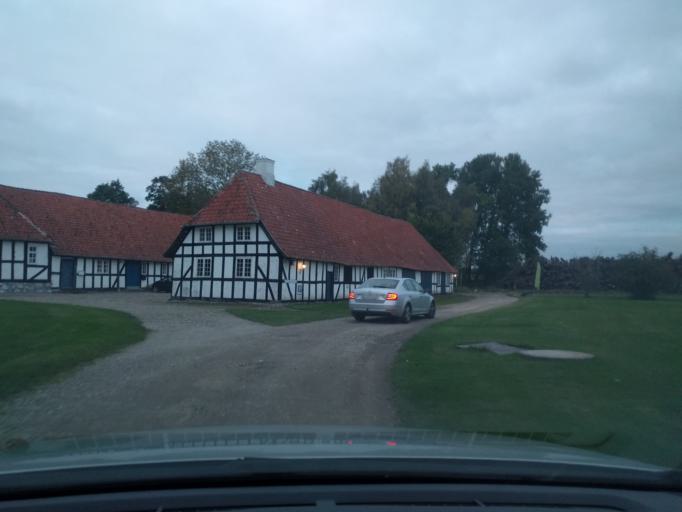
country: DK
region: South Denmark
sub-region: Assens Kommune
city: Tommerup
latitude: 55.2284
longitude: 10.2700
